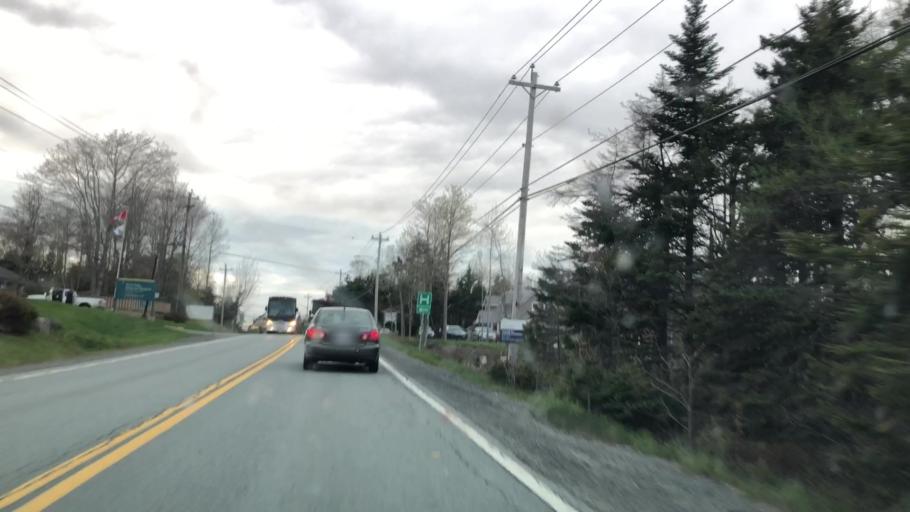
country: CA
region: Nova Scotia
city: Cole Harbour
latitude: 44.7835
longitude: -63.1579
